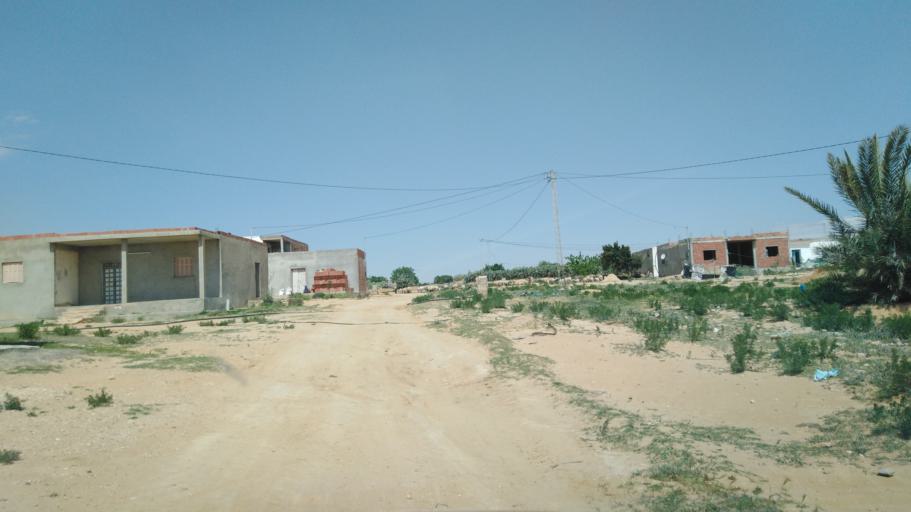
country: TN
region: Safaqis
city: Sfax
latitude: 34.7632
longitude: 10.5217
